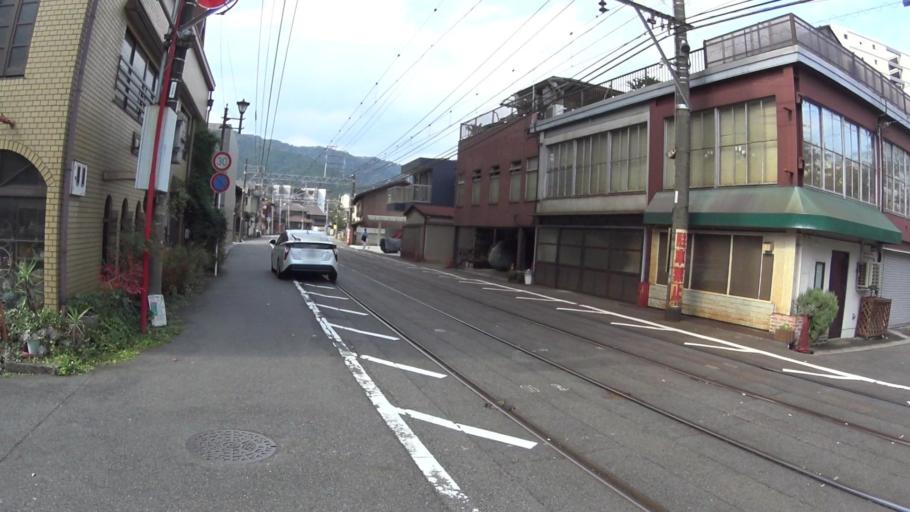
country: JP
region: Shiga Prefecture
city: Nagahama
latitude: 35.3862
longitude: 136.2251
